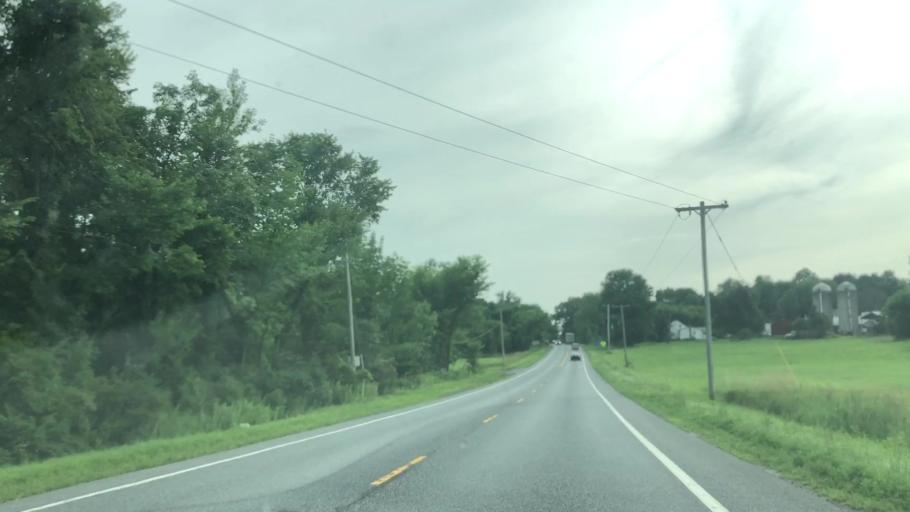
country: US
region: New York
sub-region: Warren County
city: Queensbury
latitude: 43.4108
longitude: -73.5137
